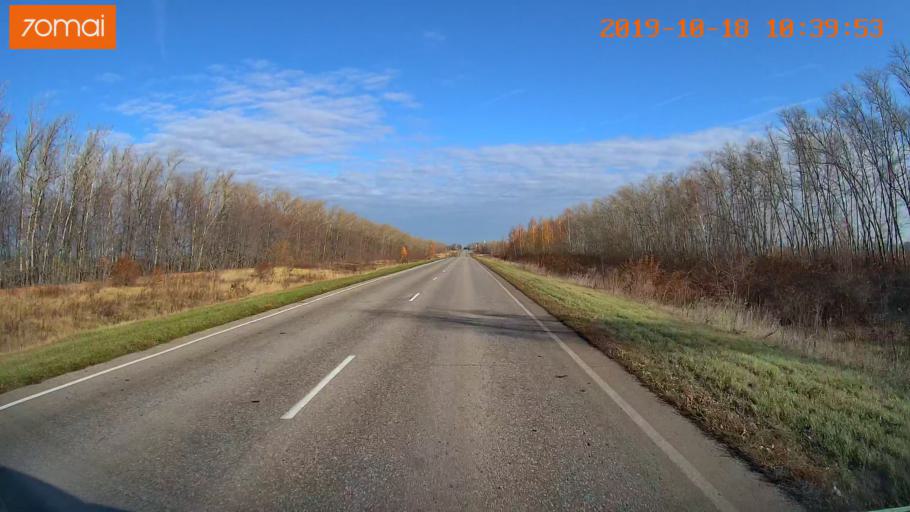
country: RU
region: Tula
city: Kurkino
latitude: 53.5931
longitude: 38.6582
